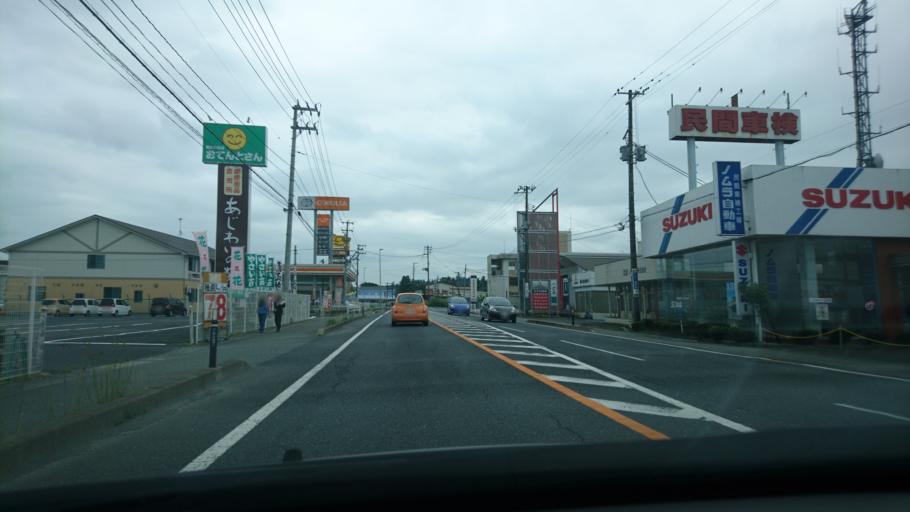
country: JP
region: Miyagi
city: Furukawa
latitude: 38.7453
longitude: 141.0151
